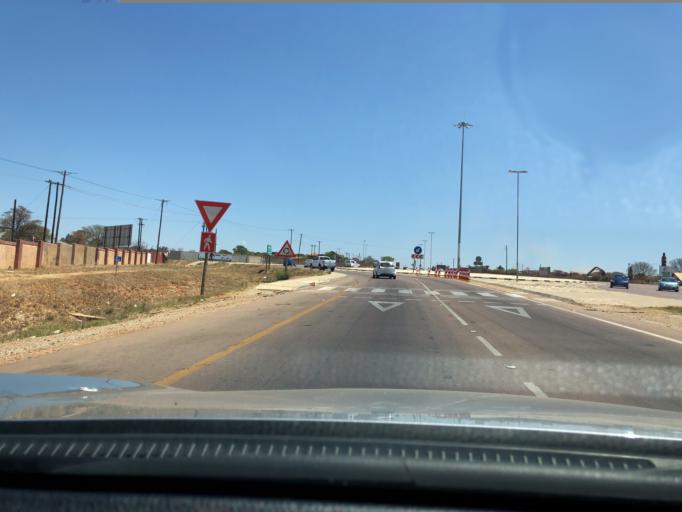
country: ZA
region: Limpopo
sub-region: Capricorn District Municipality
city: Polokwane
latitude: -23.8986
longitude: 29.5242
